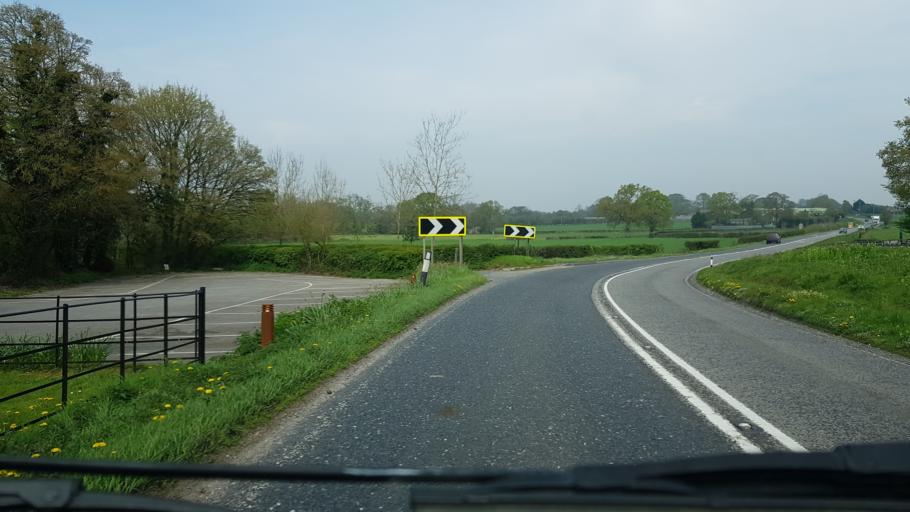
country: GB
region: England
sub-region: Hampshire
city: Kingsclere
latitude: 51.3349
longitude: -1.2590
